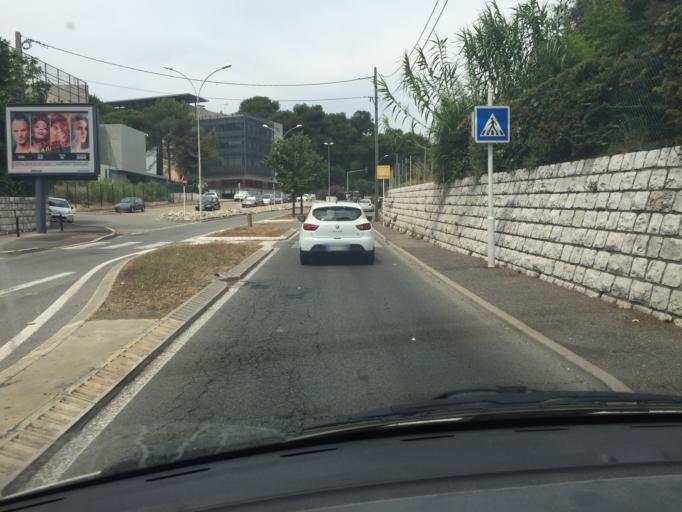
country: FR
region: Provence-Alpes-Cote d'Azur
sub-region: Departement des Alpes-Maritimes
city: Biot
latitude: 43.5931
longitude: 7.1006
